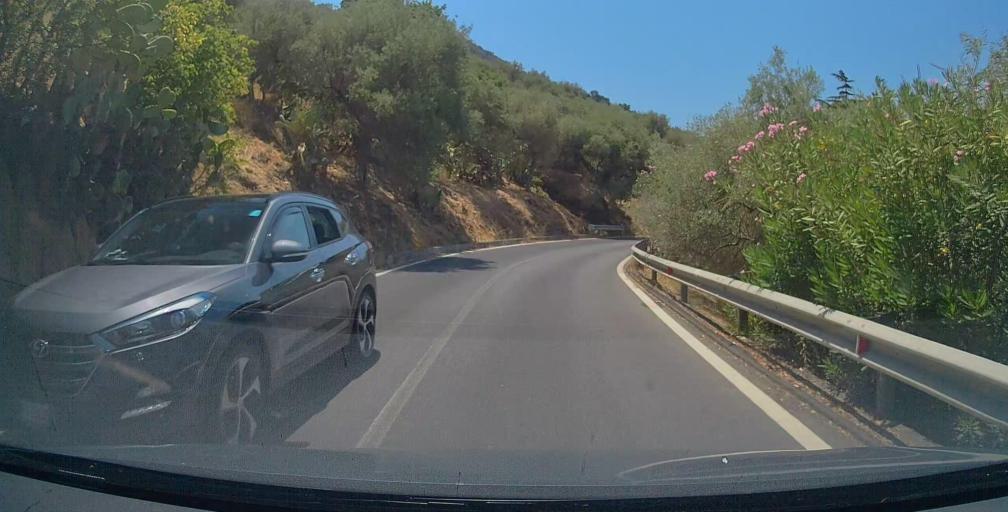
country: IT
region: Sicily
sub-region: Messina
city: Patti
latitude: 38.1404
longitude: 15.0090
